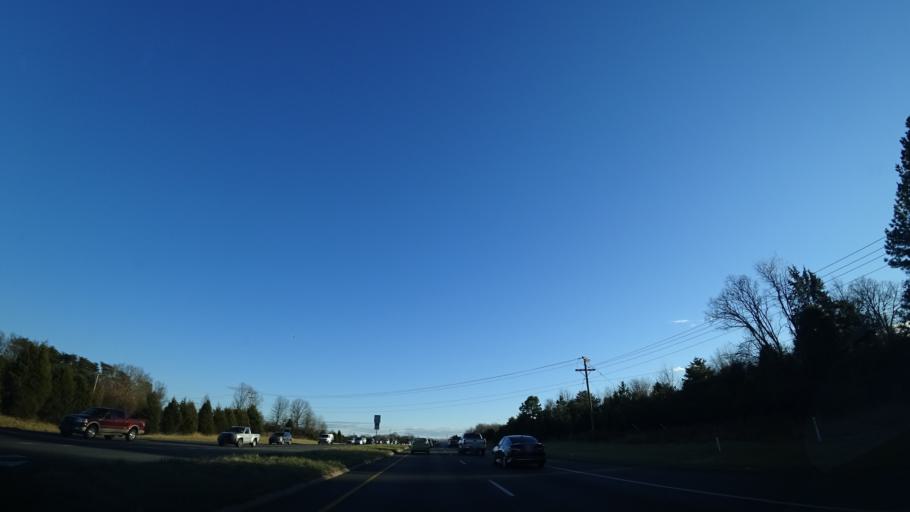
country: US
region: Virginia
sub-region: Prince William County
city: Bull Run
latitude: 38.7691
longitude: -77.5368
